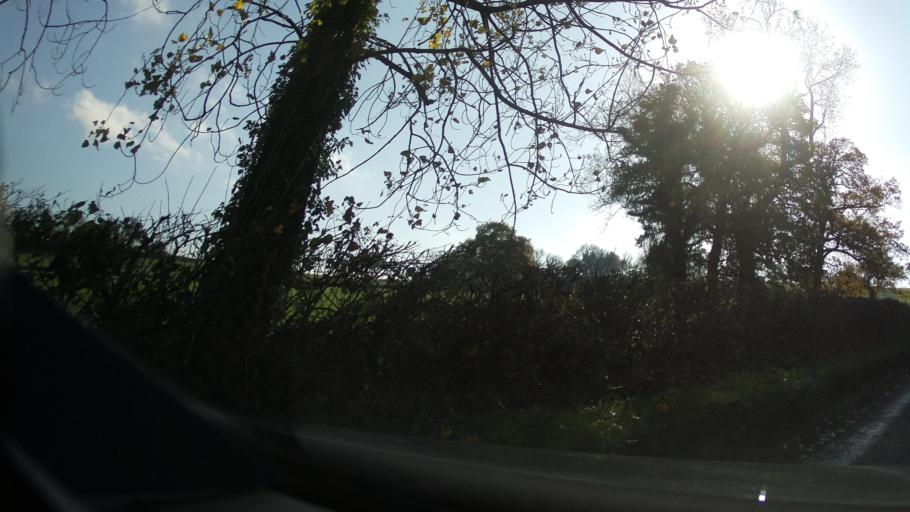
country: GB
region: England
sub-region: Somerset
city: Bruton
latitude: 51.1672
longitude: -2.4147
